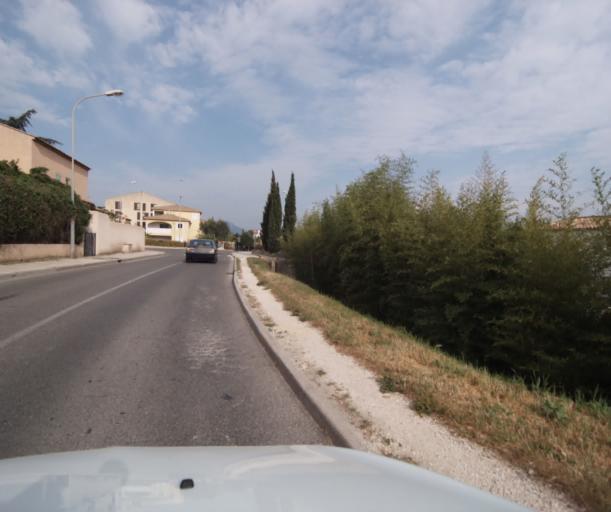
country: FR
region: Provence-Alpes-Cote d'Azur
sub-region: Departement du Var
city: Hyeres
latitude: 43.1078
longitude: 6.1187
